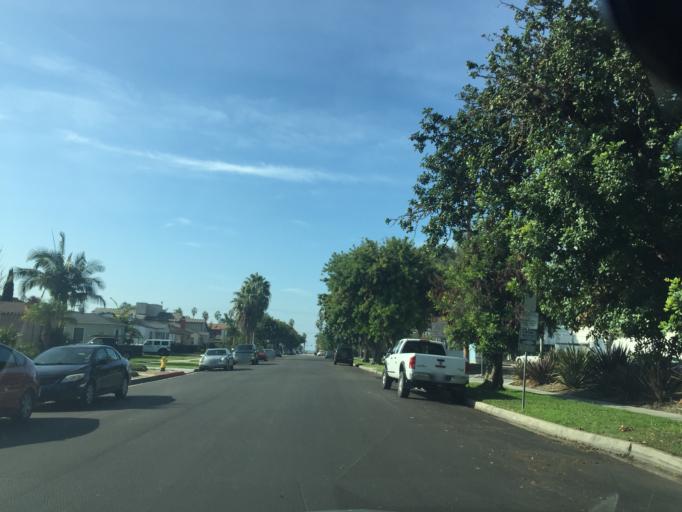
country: US
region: California
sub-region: San Diego County
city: La Jolla
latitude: 32.7939
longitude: -117.2492
